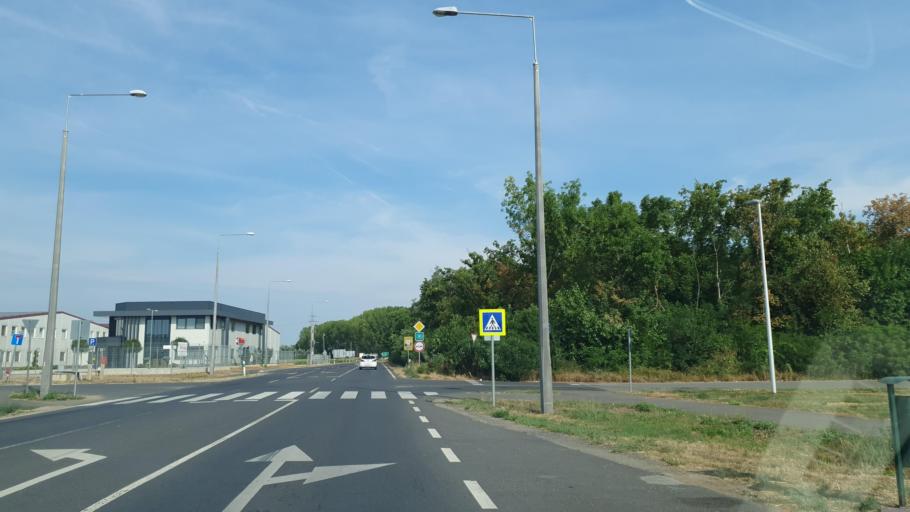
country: HU
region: Szabolcs-Szatmar-Bereg
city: Kisvarda
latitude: 48.2344
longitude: 22.0627
